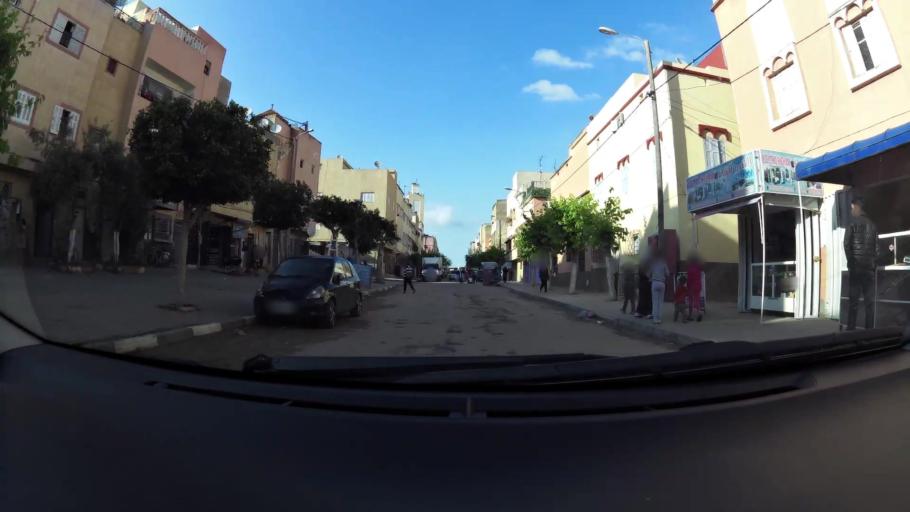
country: MA
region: Chaouia-Ouardigha
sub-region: Settat Province
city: Settat
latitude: 33.0041
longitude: -7.6257
